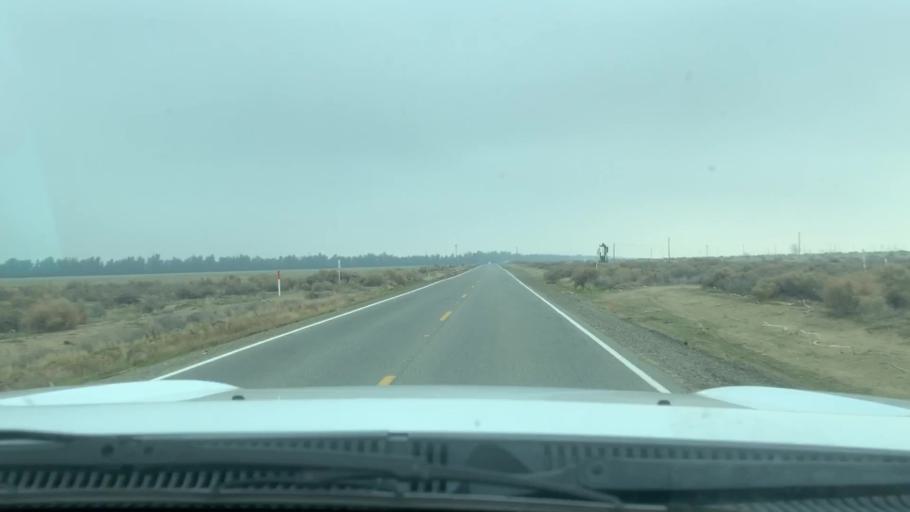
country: US
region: California
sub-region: Kern County
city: Lost Hills
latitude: 35.5343
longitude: -119.7686
